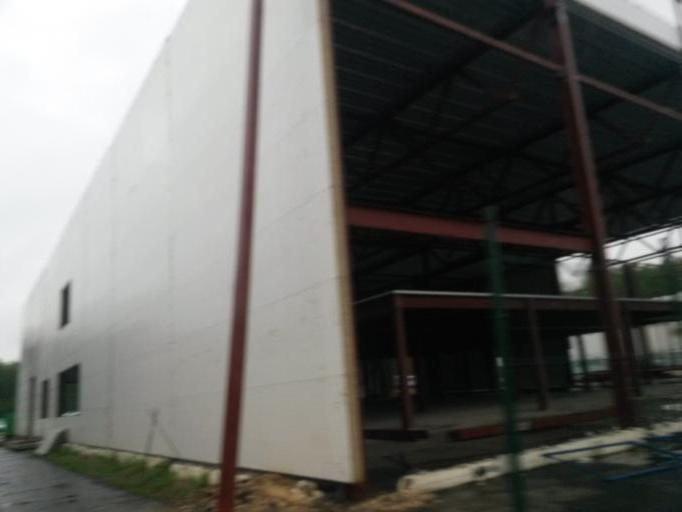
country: RU
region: Moskovskaya
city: Shcherbinka
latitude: 55.4919
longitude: 37.6099
